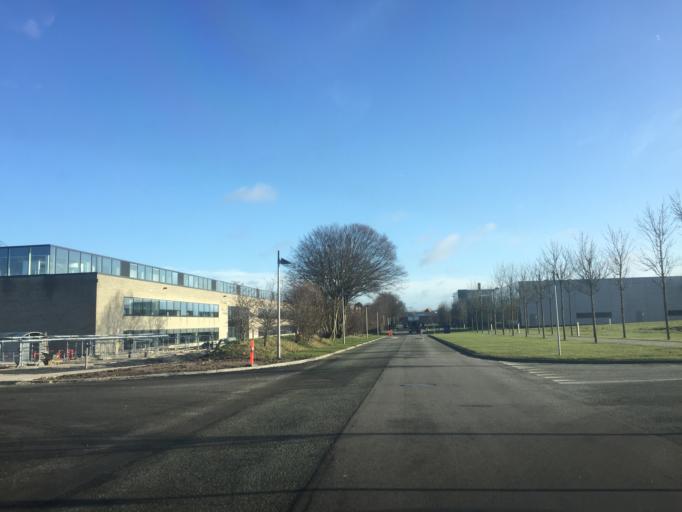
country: DK
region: Capital Region
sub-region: Hillerod Kommune
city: Hillerod
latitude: 55.9155
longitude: 12.2801
